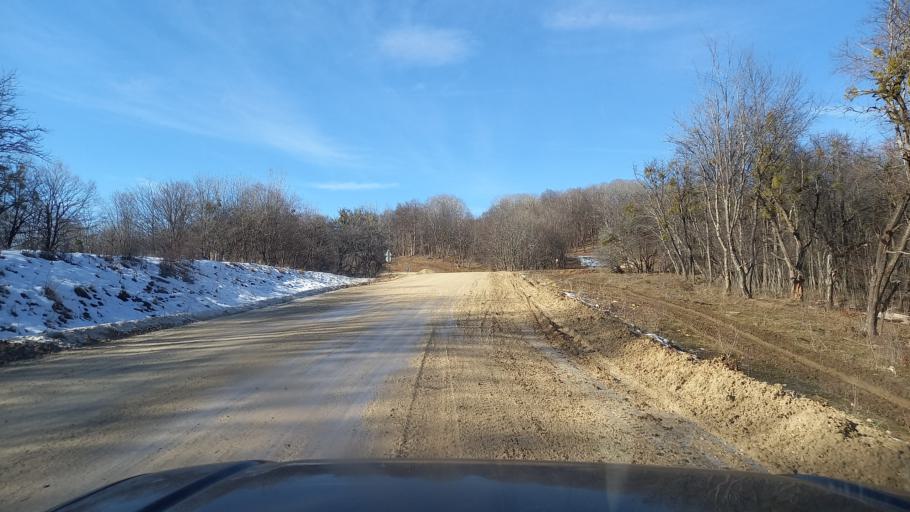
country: RU
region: Adygeya
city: Kamennomostskiy
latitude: 44.2817
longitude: 40.3223
